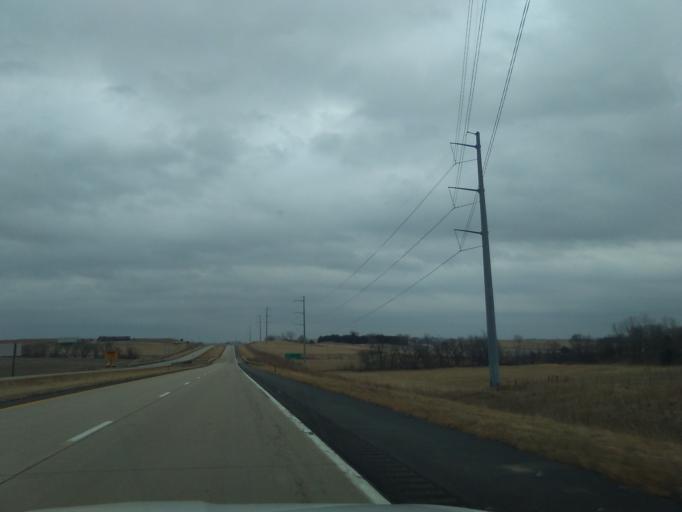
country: US
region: Nebraska
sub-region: Otoe County
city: Syracuse
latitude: 40.6704
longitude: -96.1688
